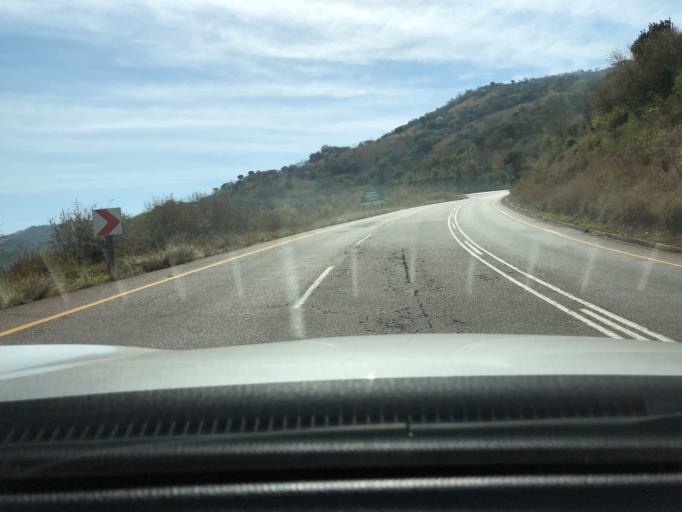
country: ZA
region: KwaZulu-Natal
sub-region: uMgungundlovu District Municipality
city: Richmond
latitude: -30.0025
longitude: 30.2444
